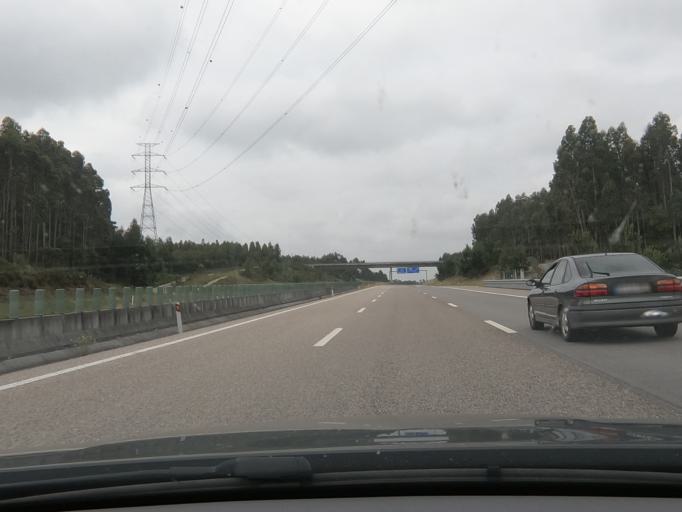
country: PT
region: Coimbra
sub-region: Figueira da Foz
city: Lavos
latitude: 40.0599
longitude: -8.7994
